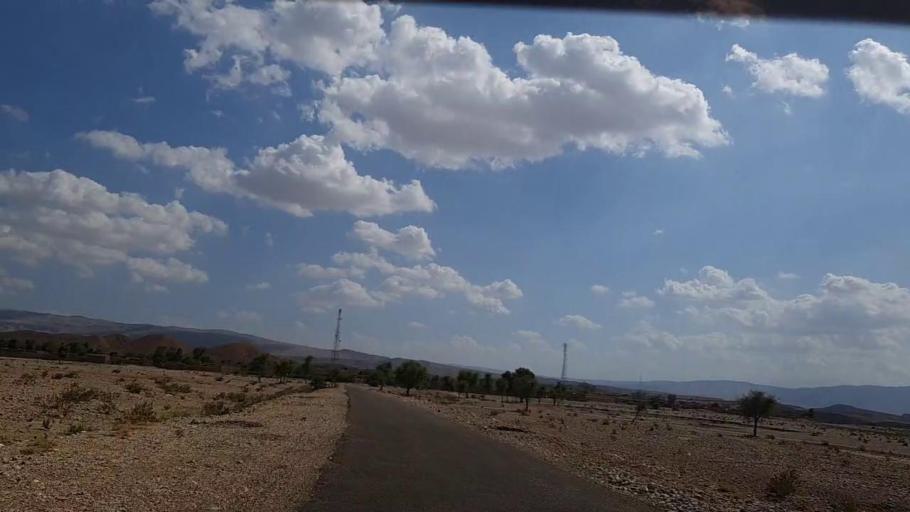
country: PK
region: Sindh
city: Johi
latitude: 26.5009
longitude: 67.4359
